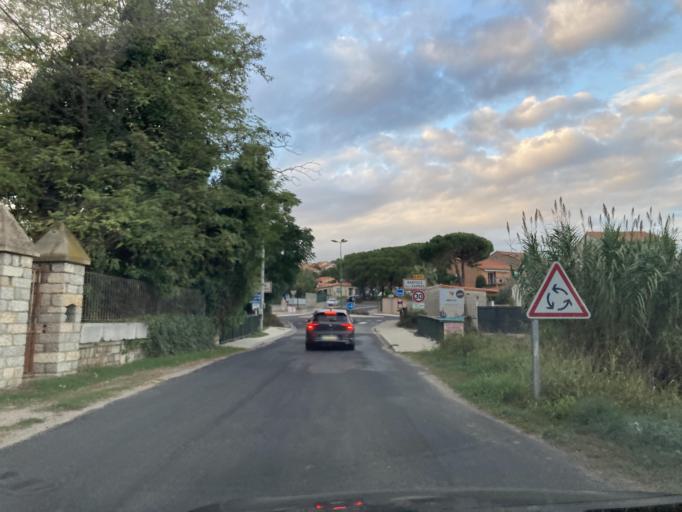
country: FR
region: Languedoc-Roussillon
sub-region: Departement des Pyrenees-Orientales
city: Banyuls-dels-Aspres
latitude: 42.5617
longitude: 2.8710
